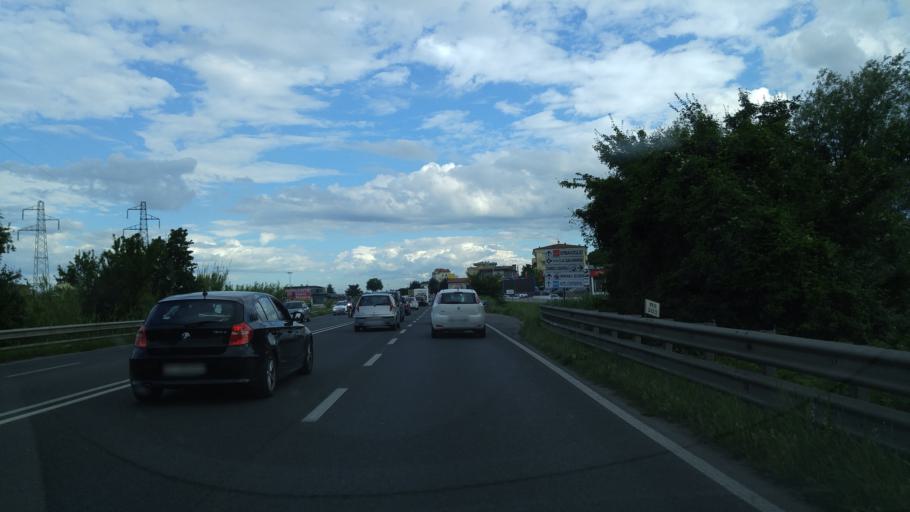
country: IT
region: Emilia-Romagna
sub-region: Provincia di Rimini
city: Rimini
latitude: 44.0488
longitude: 12.5494
